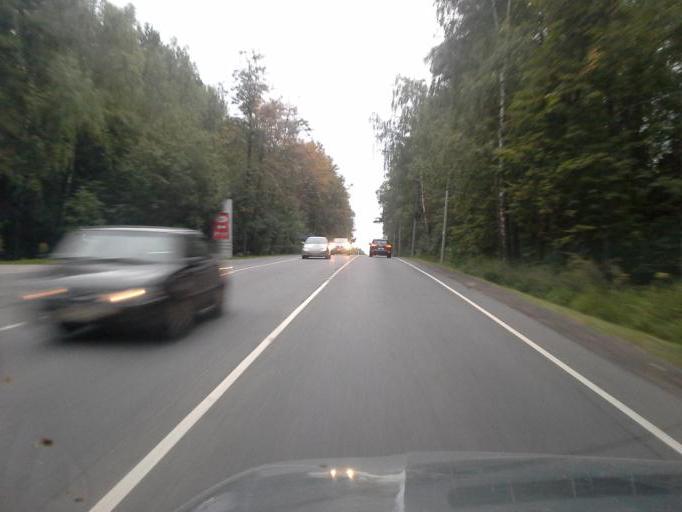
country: RU
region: Moskovskaya
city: Nazar'yevo
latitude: 55.6843
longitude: 37.0750
